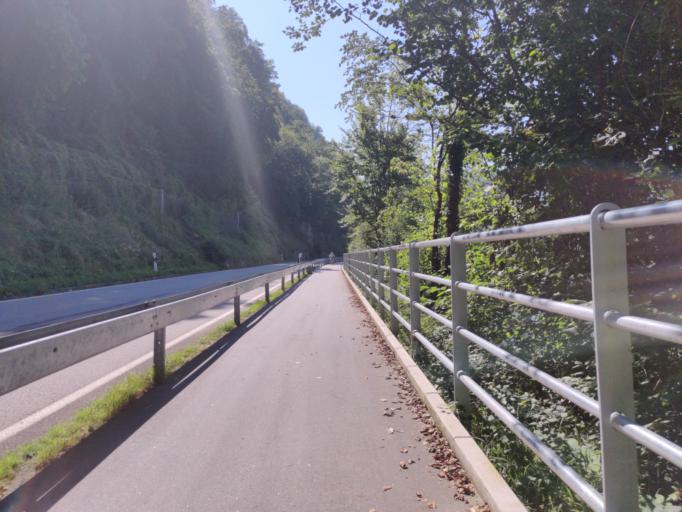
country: DE
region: Bavaria
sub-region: Lower Bavaria
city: Obernzell
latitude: 48.5455
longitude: 13.6579
